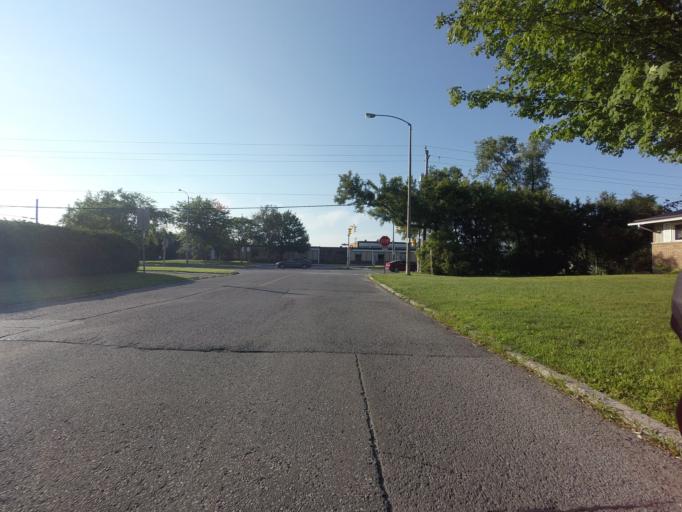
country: CA
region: Ontario
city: Bells Corners
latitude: 45.3271
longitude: -75.7685
